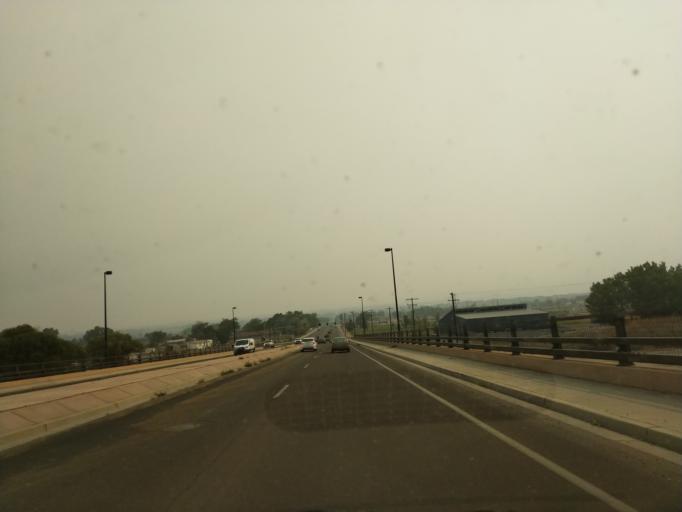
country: US
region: Colorado
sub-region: Mesa County
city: Fruitvale
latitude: 39.0708
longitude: -108.5155
